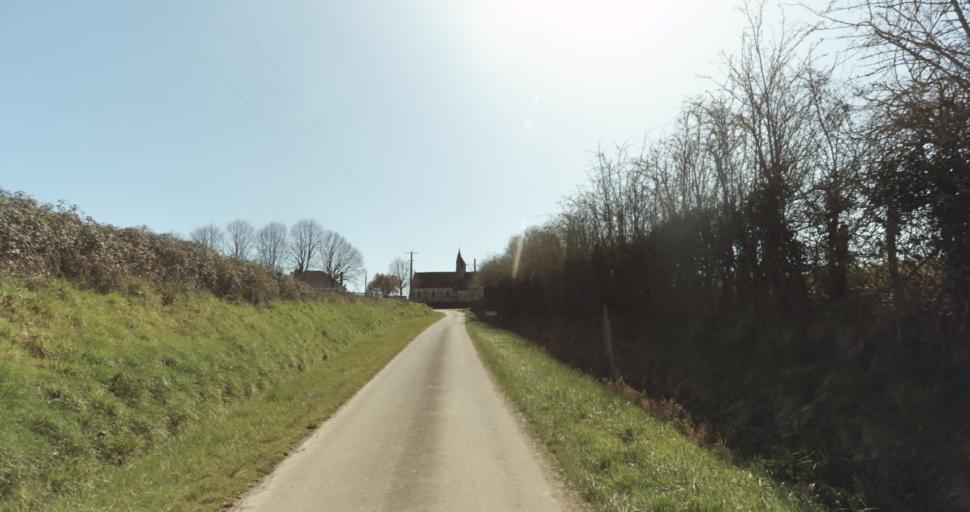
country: FR
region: Lower Normandy
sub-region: Departement du Calvados
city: Saint-Pierre-sur-Dives
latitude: 49.0104
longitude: 0.0226
